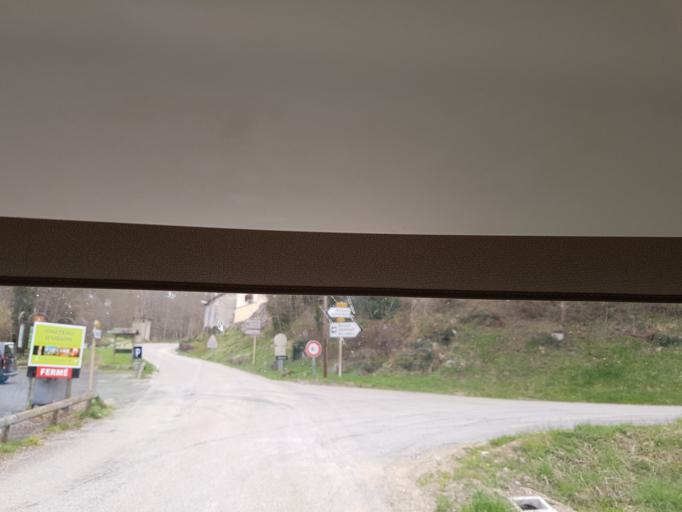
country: FR
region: Languedoc-Roussillon
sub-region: Departement de l'Aude
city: Quillan
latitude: 42.7352
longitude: 2.0856
